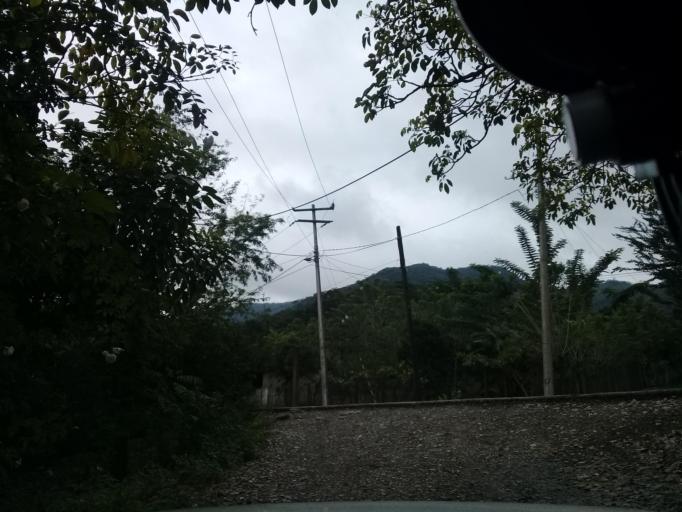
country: MX
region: Veracruz
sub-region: Chalma
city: San Pedro Coyutla
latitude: 21.2210
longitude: -98.4298
